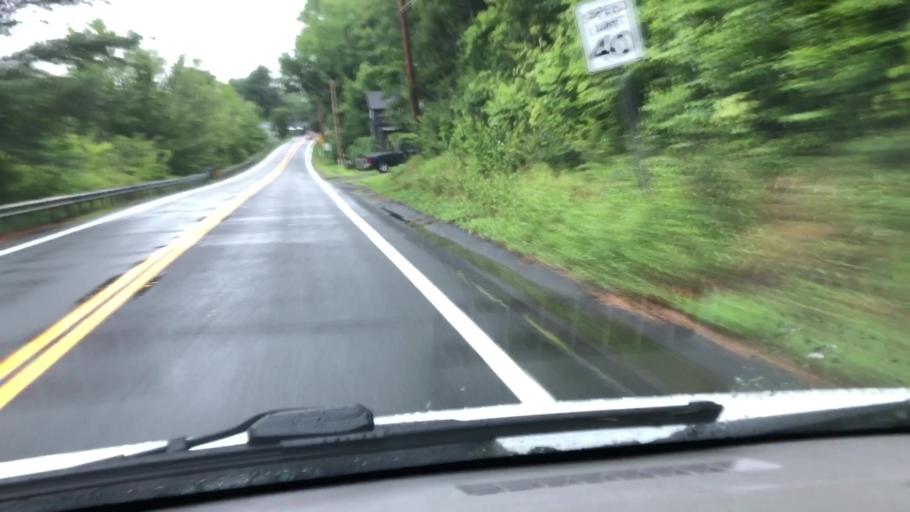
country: US
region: Massachusetts
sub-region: Hampshire County
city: Chesterfield
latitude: 42.3665
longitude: -72.9092
